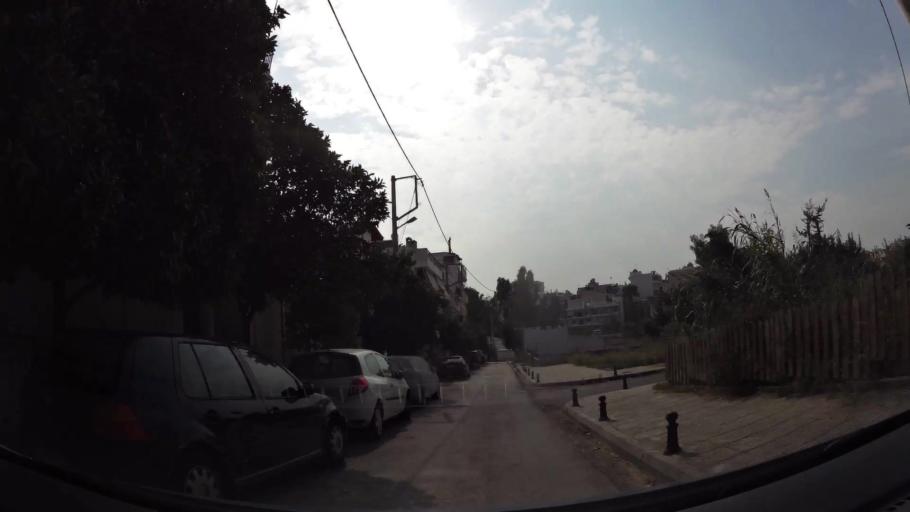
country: GR
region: Attica
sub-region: Nomarchia Athinas
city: Agios Dimitrios
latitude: 37.9331
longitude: 23.7394
